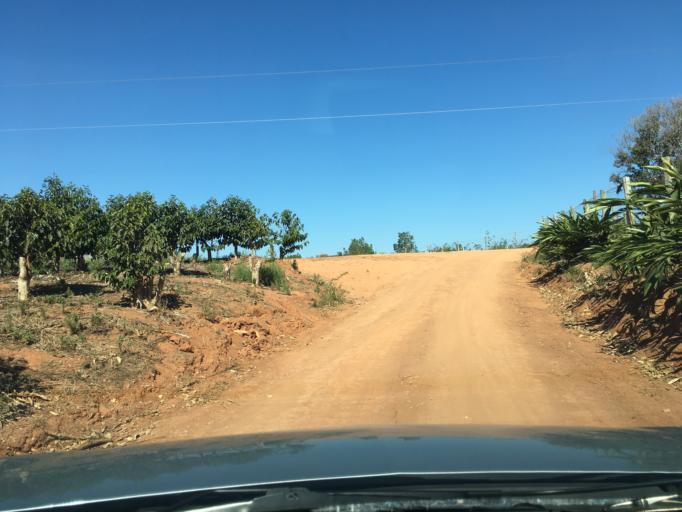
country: BR
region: Minas Gerais
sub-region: Campestre
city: Campestre
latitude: -21.5916
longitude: -46.2065
